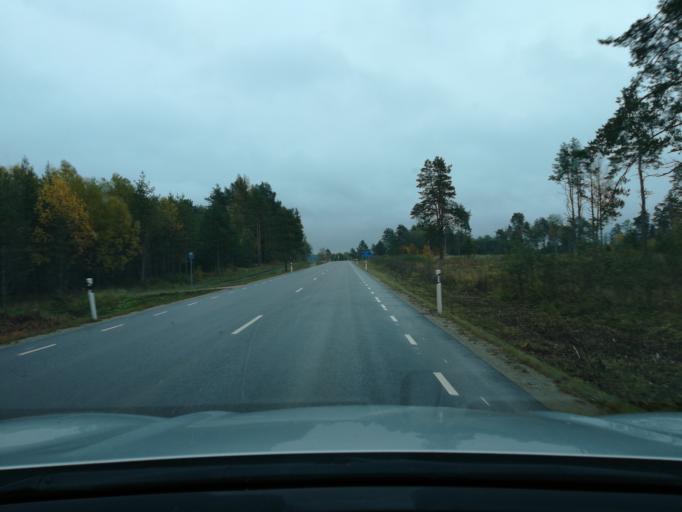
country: EE
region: Ida-Virumaa
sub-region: Johvi vald
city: Johvi
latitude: 59.2962
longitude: 27.4865
